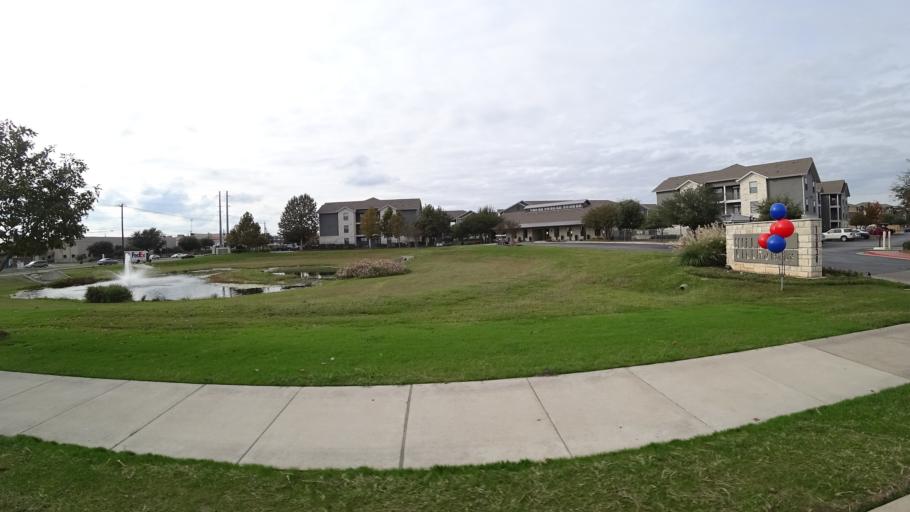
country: US
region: Texas
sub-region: Travis County
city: Wells Branch
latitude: 30.4222
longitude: -97.6656
